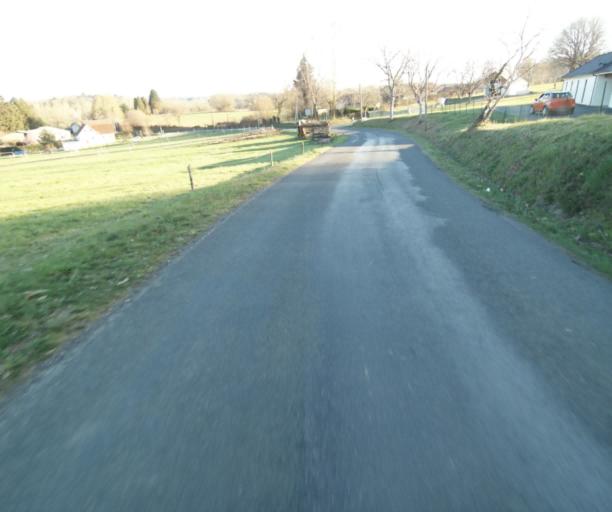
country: FR
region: Limousin
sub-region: Departement de la Correze
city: Saint-Clement
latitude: 45.3458
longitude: 1.6646
